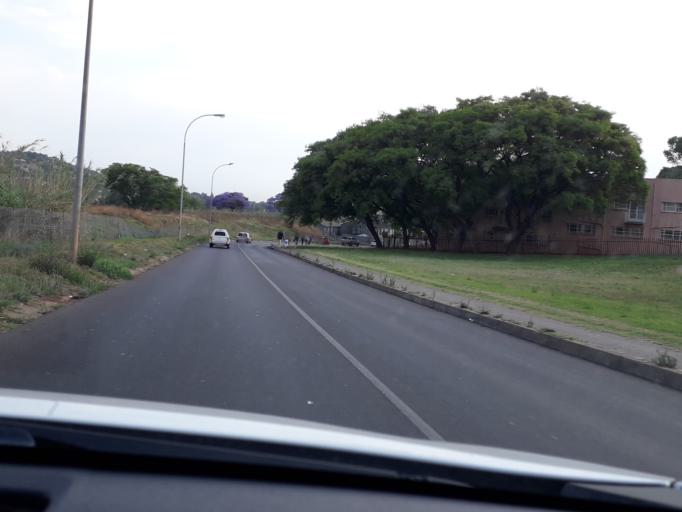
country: ZA
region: Gauteng
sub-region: City of Johannesburg Metropolitan Municipality
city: Johannesburg
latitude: -26.1684
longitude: 27.9751
